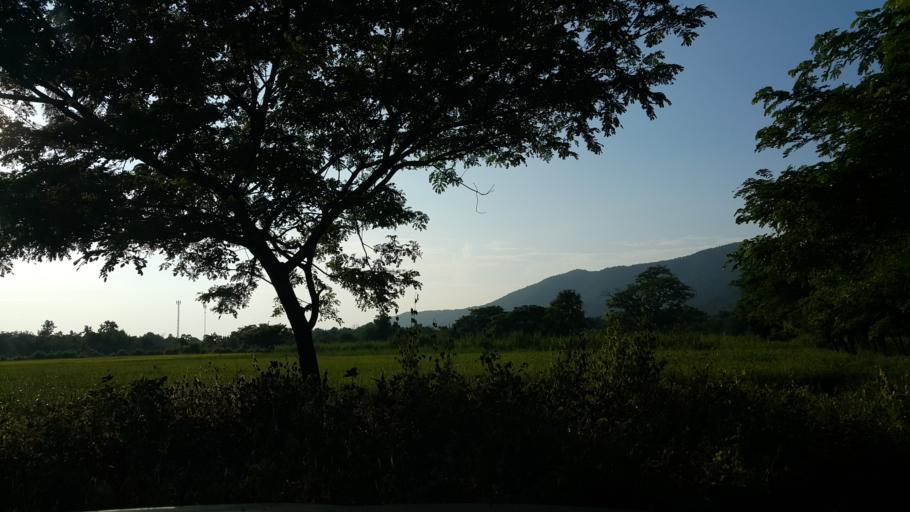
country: TH
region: Chiang Mai
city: Mae On
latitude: 18.7433
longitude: 99.2356
